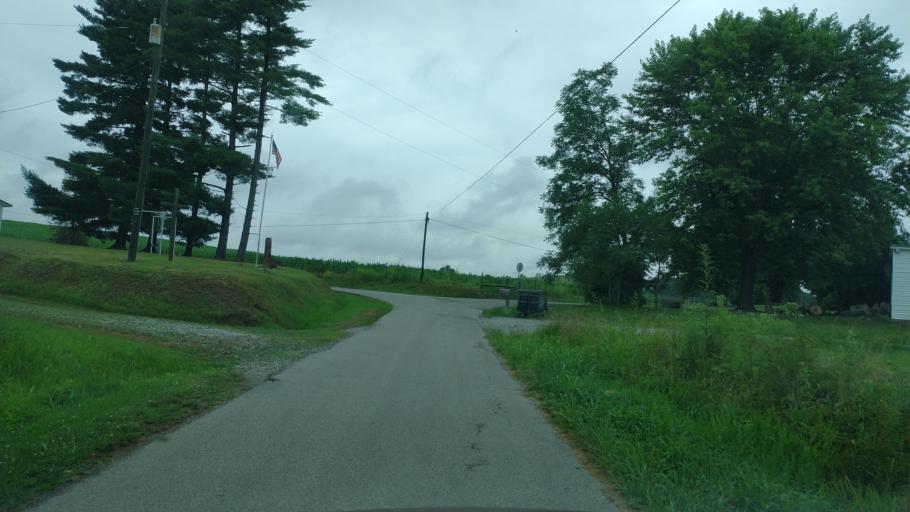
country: US
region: West Virginia
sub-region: Mason County
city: New Haven
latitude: 38.9258
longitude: -81.9597
